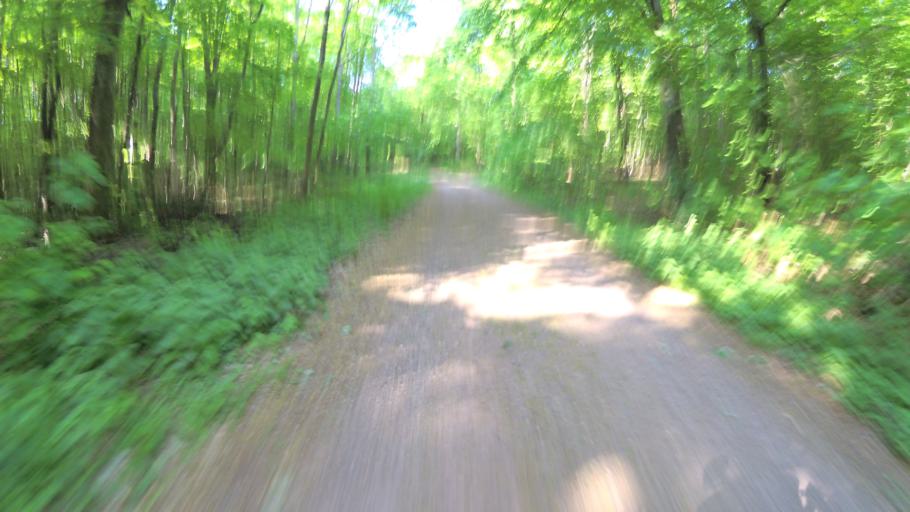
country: DE
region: Saarland
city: Marpingen
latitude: 49.4192
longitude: 7.0492
